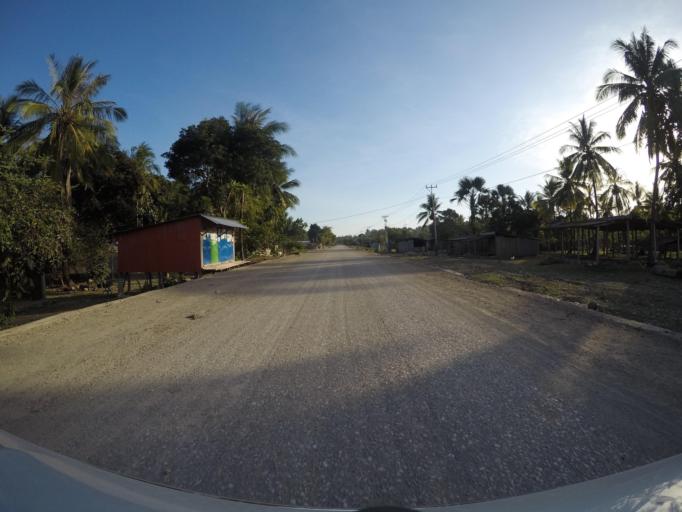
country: TL
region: Viqueque
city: Viqueque
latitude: -8.8108
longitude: 126.5391
